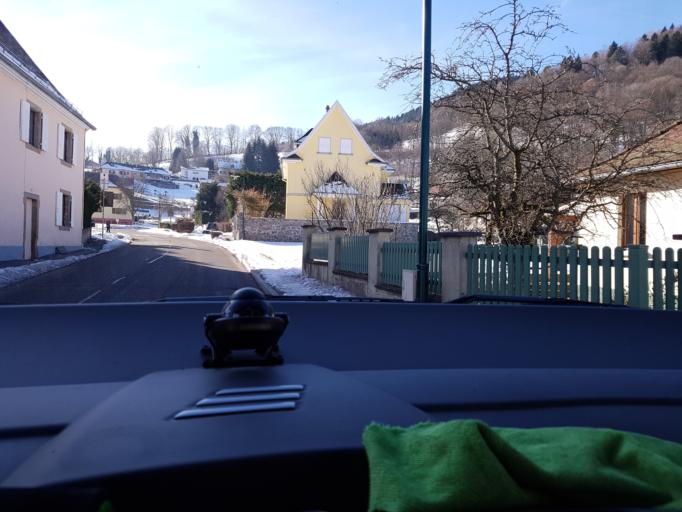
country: FR
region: Alsace
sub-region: Departement du Haut-Rhin
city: Metzeral
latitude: 48.0084
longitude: 7.0712
